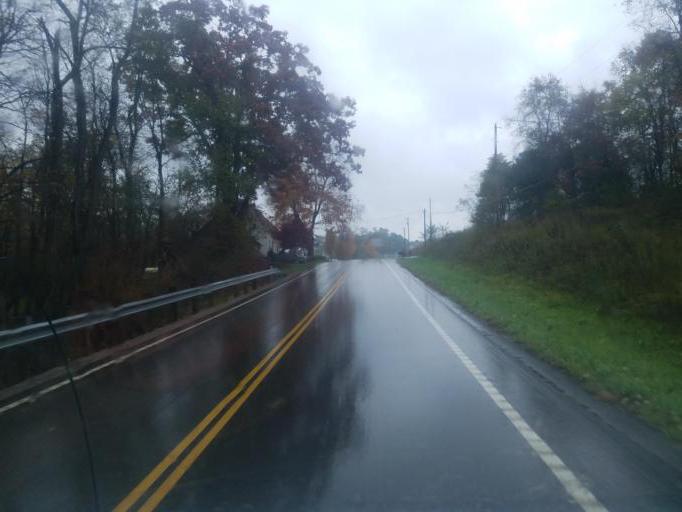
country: US
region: Ohio
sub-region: Licking County
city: Utica
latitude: 40.2336
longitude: -82.2821
